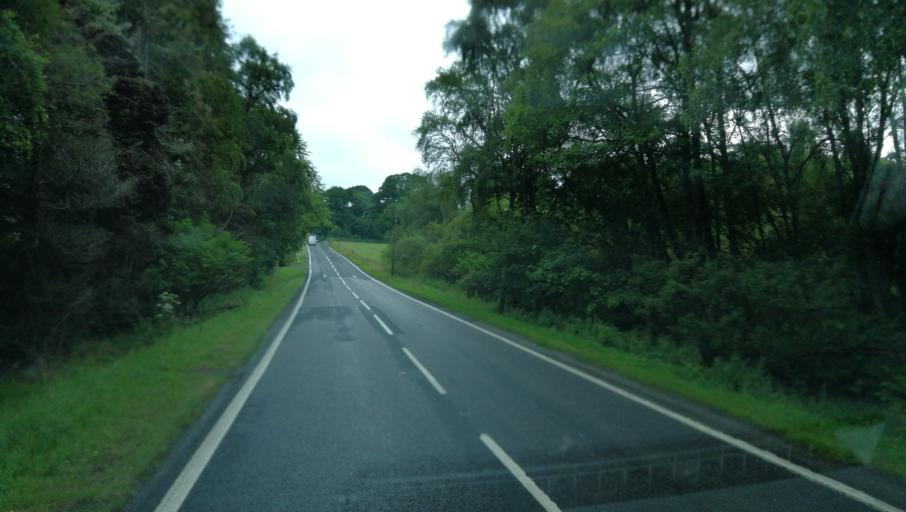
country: GB
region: Scotland
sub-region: Highland
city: Inverness
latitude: 57.4406
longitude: -4.2980
